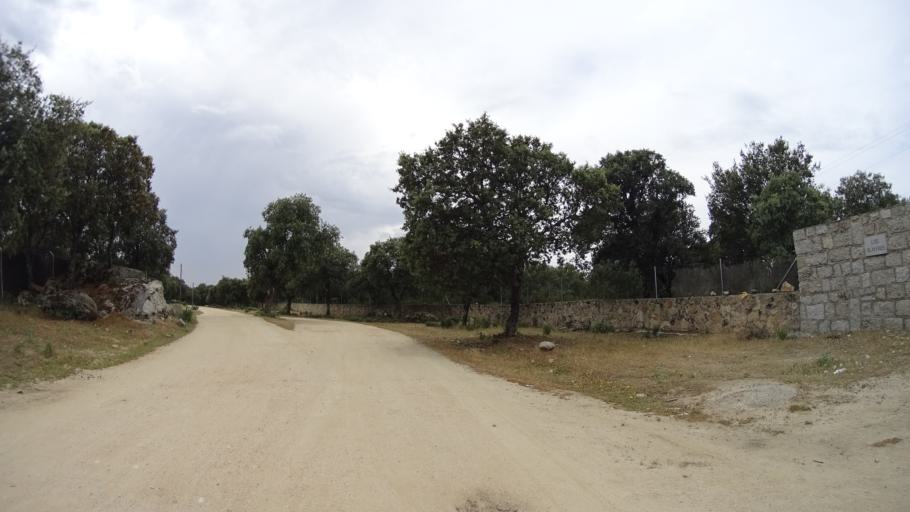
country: ES
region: Madrid
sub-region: Provincia de Madrid
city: Colmenarejo
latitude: 40.5623
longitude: -4.0348
